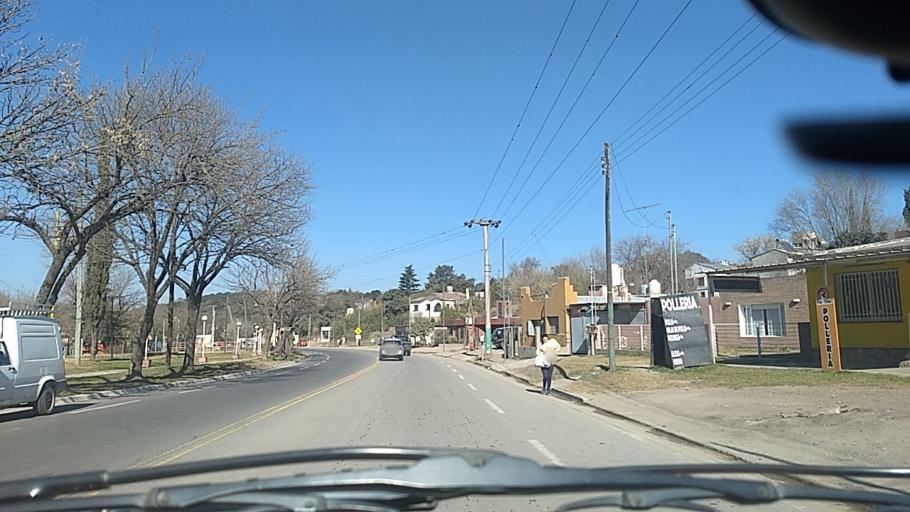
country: AR
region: Cordoba
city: Salsipuedes
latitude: -31.1057
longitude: -64.2921
